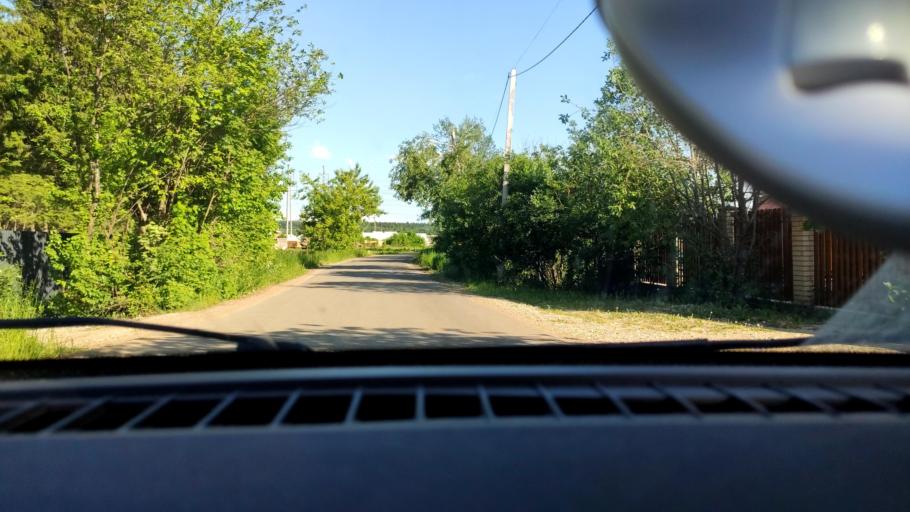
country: RU
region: Perm
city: Ferma
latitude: 57.9174
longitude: 56.3381
